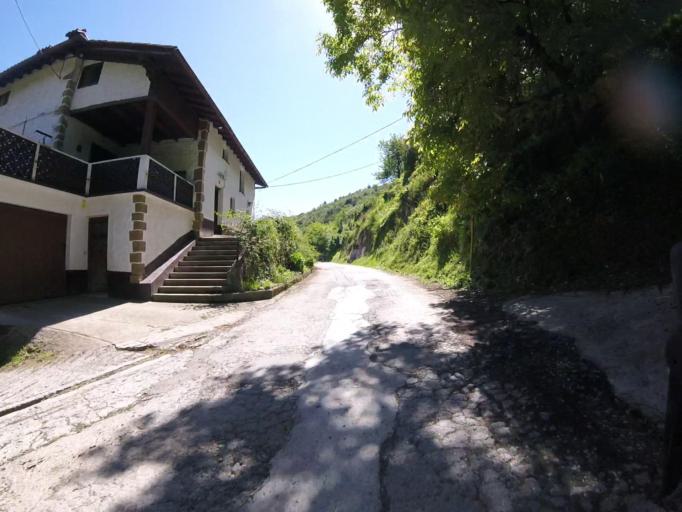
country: ES
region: Navarre
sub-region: Provincia de Navarra
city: Bera
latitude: 43.2750
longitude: -1.7122
